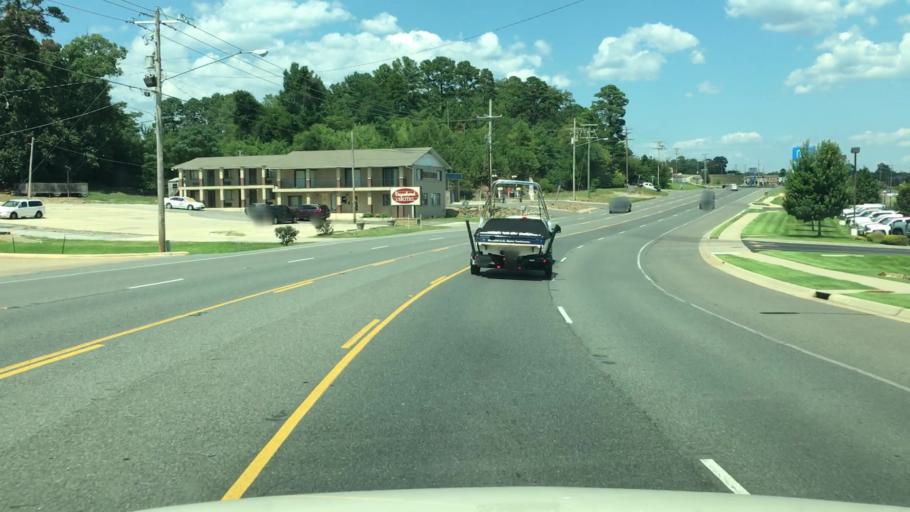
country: US
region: Arkansas
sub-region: Garland County
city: Lake Hamilton
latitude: 34.4463
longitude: -93.0896
